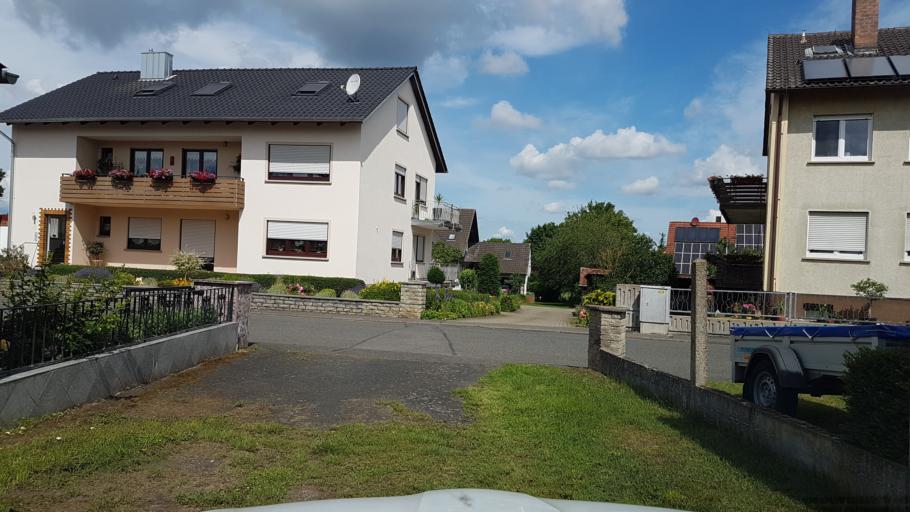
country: DE
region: Bavaria
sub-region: Regierungsbezirk Unterfranken
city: Kleinlangheim
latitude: 49.8127
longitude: 10.2945
